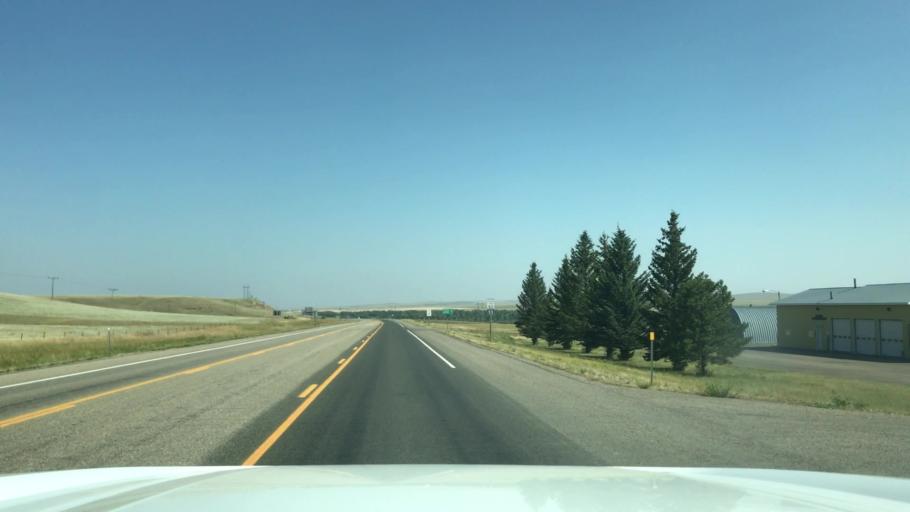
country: US
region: Montana
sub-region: Wheatland County
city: Harlowton
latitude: 46.4345
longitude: -109.8095
